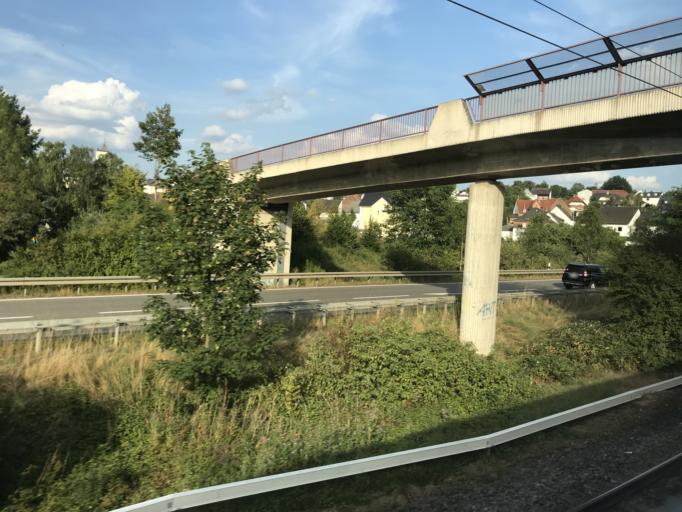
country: DE
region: Hesse
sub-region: Regierungsbezirk Giessen
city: Villmar
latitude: 50.3513
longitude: 8.1931
